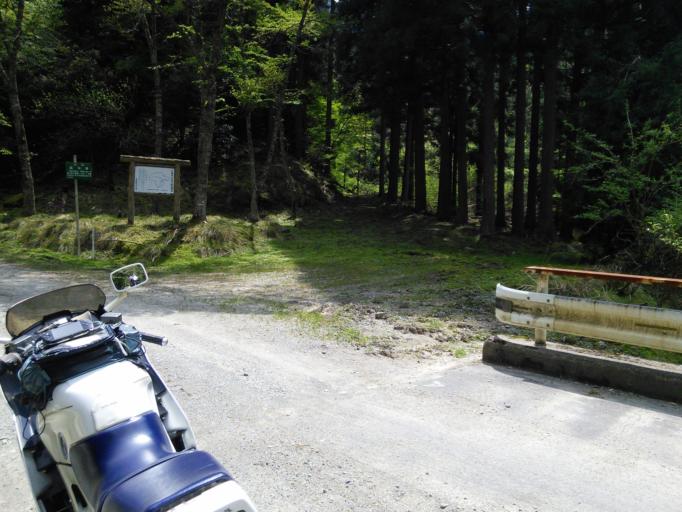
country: JP
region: Kyoto
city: Ayabe
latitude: 35.2441
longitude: 135.4914
